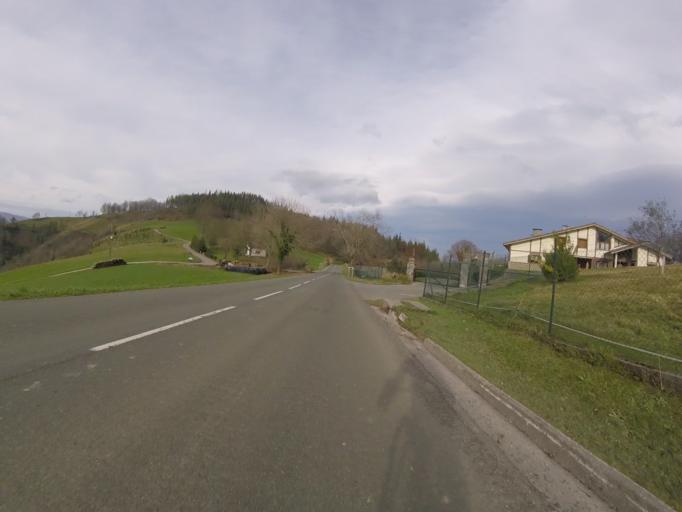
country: ES
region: Basque Country
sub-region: Provincia de Guipuzcoa
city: Beizama
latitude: 43.1550
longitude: -2.2047
